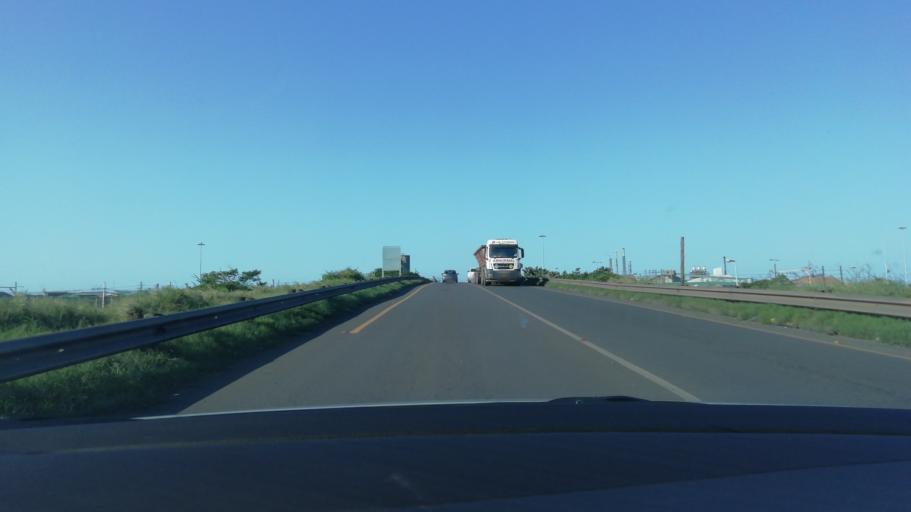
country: ZA
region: KwaZulu-Natal
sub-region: uThungulu District Municipality
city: Richards Bay
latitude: -28.7847
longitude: 32.0272
